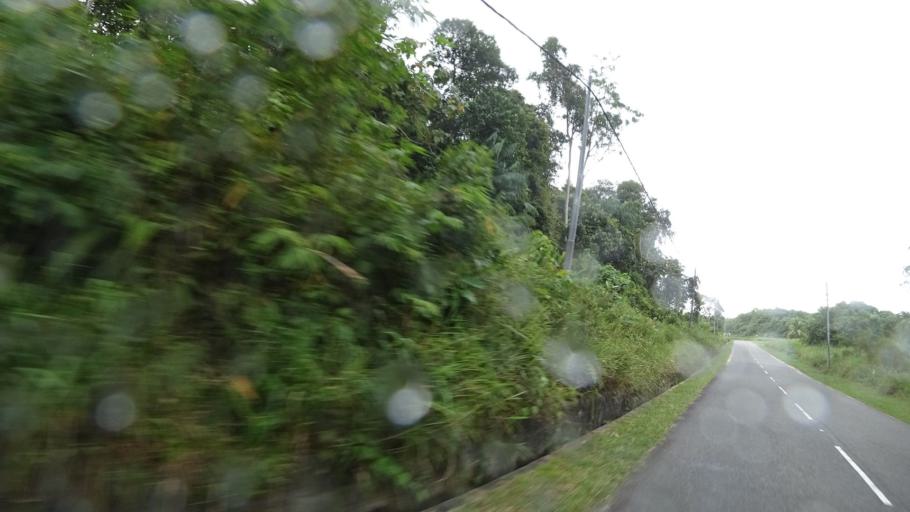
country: BN
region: Brunei and Muara
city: Bandar Seri Begawan
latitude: 4.8505
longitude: 114.9539
